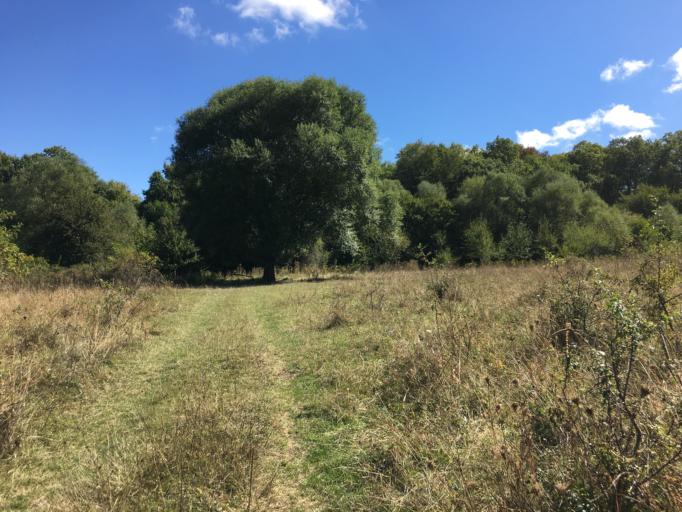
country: GE
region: Mtskheta-Mtianeti
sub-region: Tianetis Munitsip'alit'et'i
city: T'ianet'i
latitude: 41.9363
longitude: 44.9757
